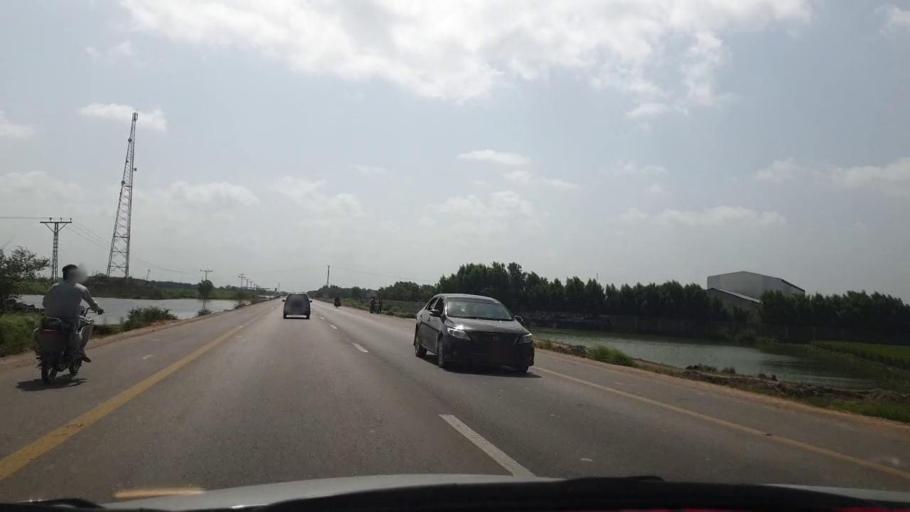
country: PK
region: Sindh
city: Matli
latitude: 24.9366
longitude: 68.7078
